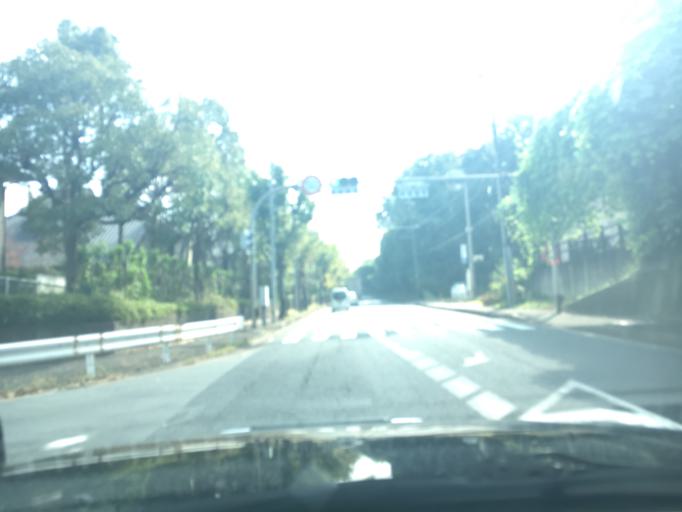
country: JP
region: Nara
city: Nara-shi
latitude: 34.7080
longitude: 135.8310
